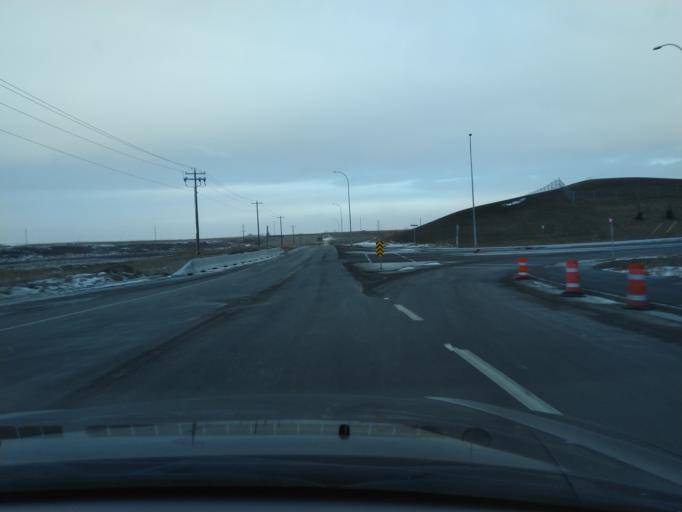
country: CA
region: Alberta
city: Calgary
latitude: 51.1648
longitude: -114.0248
